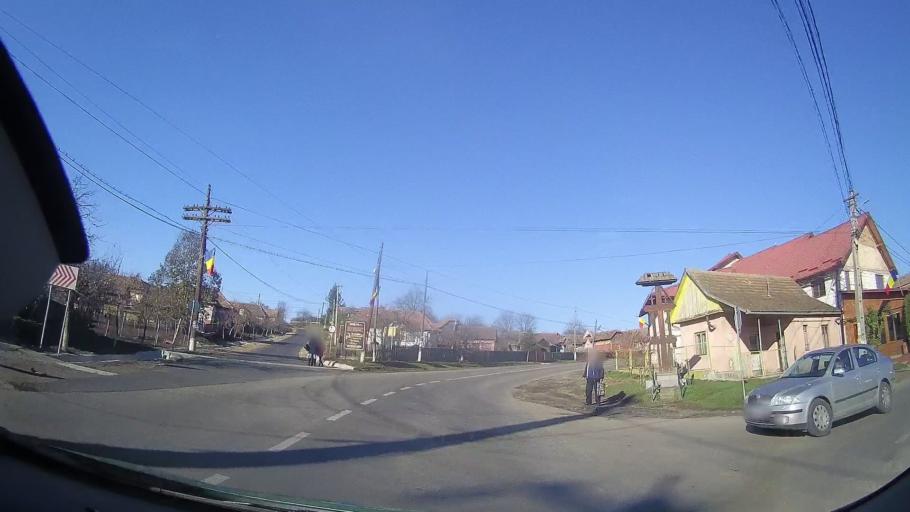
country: RO
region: Mures
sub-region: Comuna Saulia
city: Saulia
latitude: 46.6441
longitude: 24.2148
